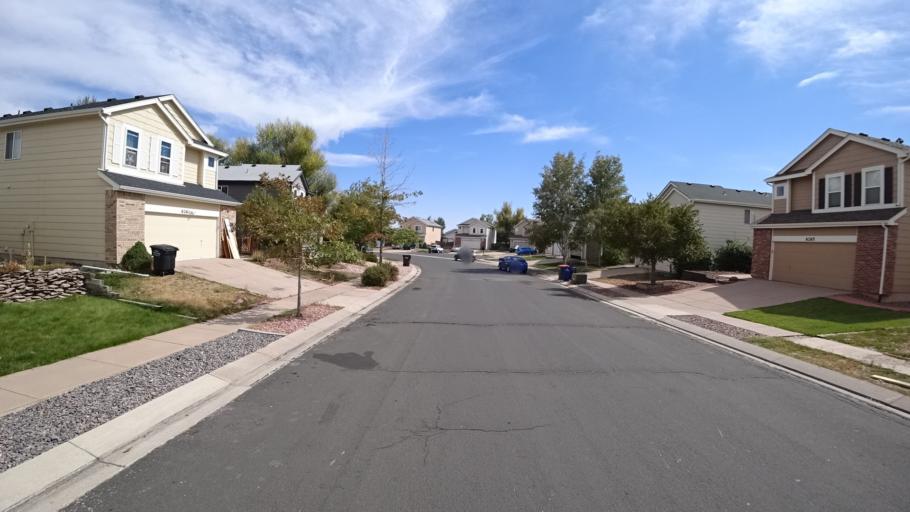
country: US
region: Colorado
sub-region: El Paso County
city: Cimarron Hills
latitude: 38.9067
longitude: -104.7111
